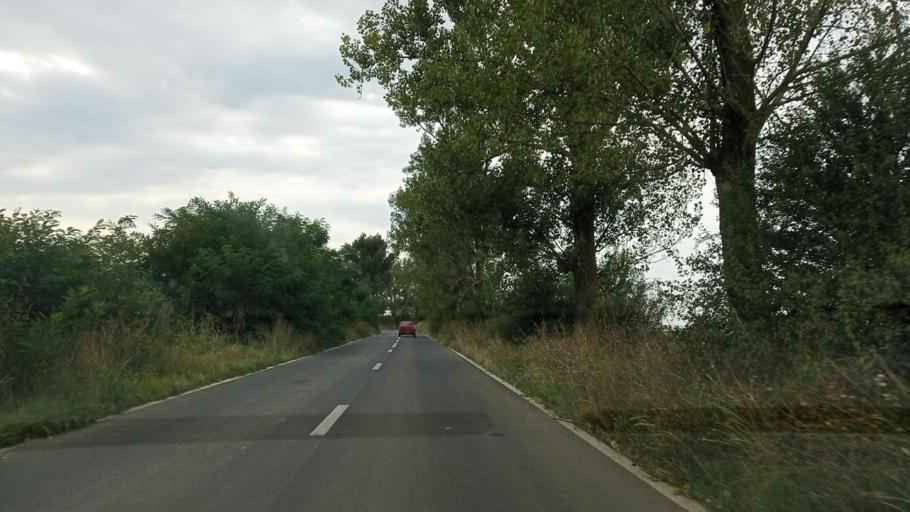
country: RO
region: Giurgiu
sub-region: Comuna Gostinari
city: Gostinari
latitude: 44.1732
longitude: 26.2303
